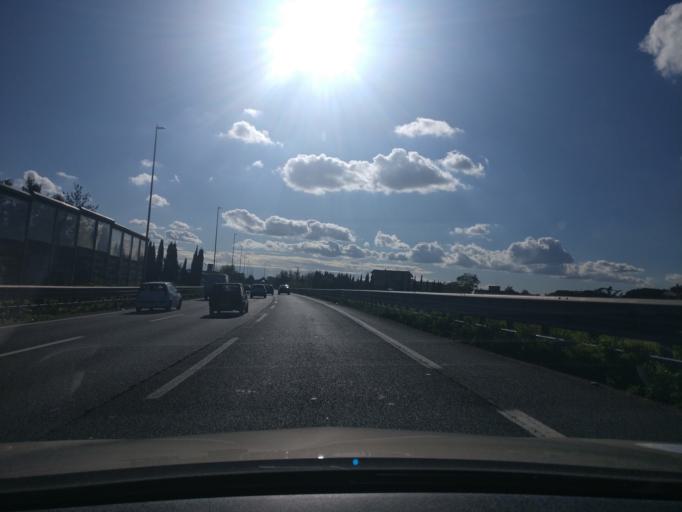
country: IT
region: Latium
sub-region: Citta metropolitana di Roma Capitale
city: Ciampino
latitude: 41.8312
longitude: 12.5835
